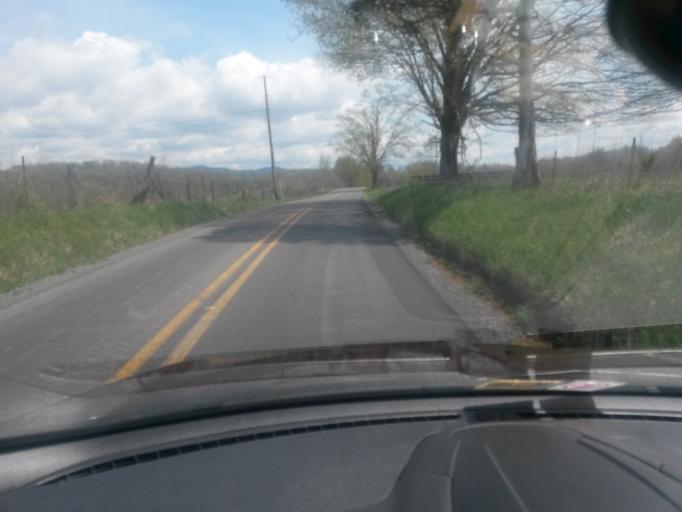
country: US
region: West Virginia
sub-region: Pocahontas County
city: Marlinton
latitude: 38.1051
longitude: -80.2256
